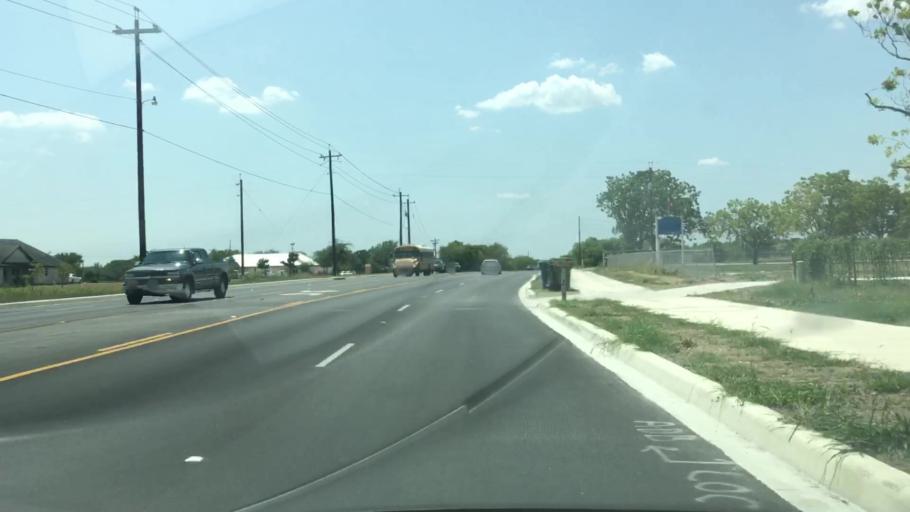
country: US
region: Texas
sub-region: Guadalupe County
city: Cibolo
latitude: 29.5695
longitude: -98.2439
